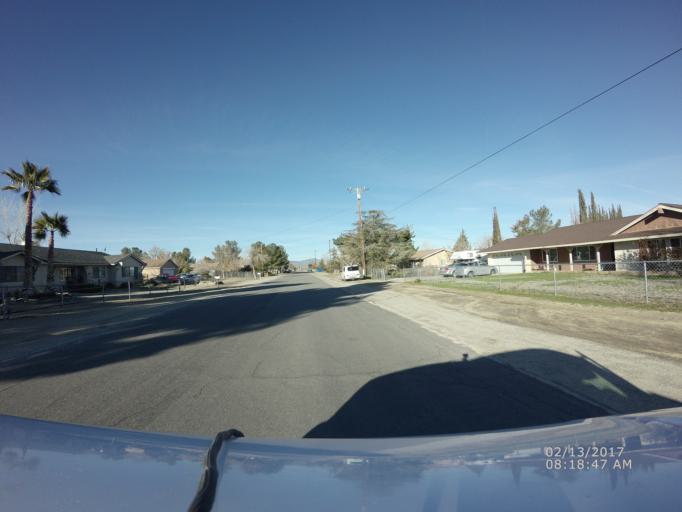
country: US
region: California
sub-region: Los Angeles County
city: Littlerock
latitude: 34.5393
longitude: -117.9683
